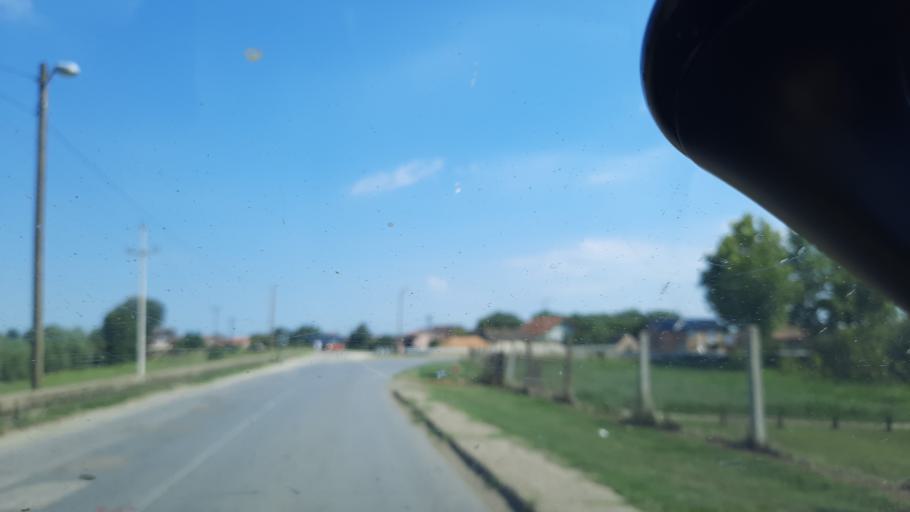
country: RS
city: Macvanska Mitrovica
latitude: 44.9602
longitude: 19.6043
